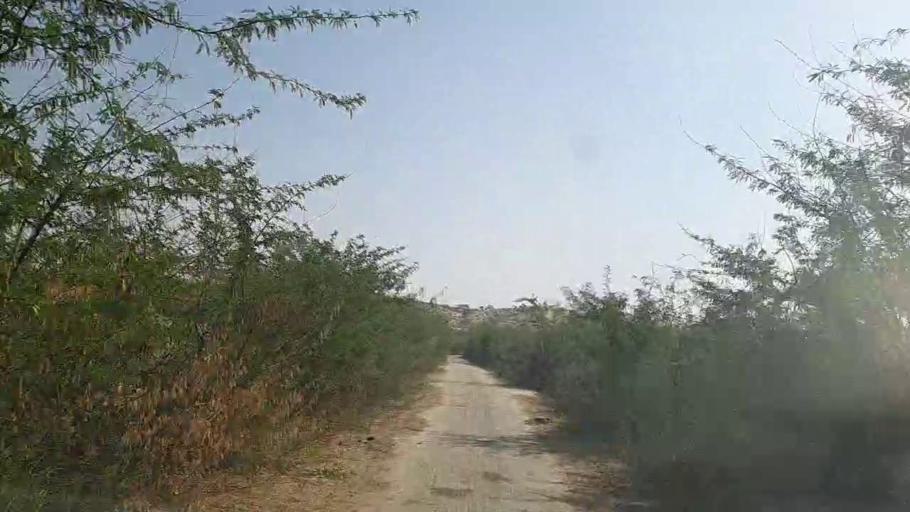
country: PK
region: Sindh
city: Naukot
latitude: 24.5710
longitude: 69.2923
